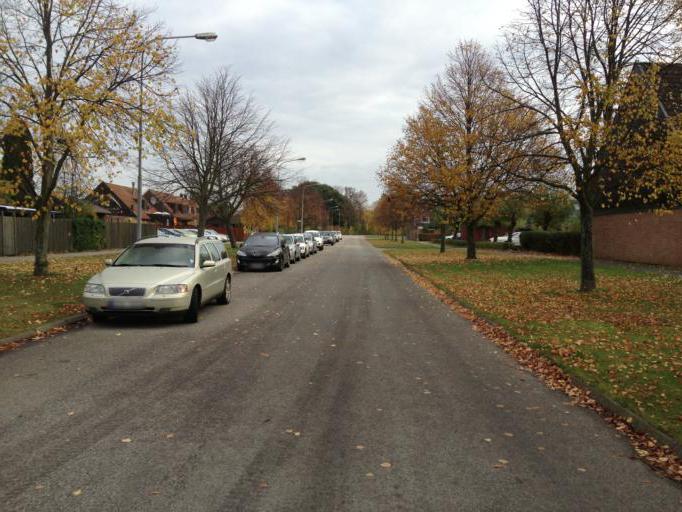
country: SE
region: Skane
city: Bjarred
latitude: 55.7260
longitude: 13.0070
